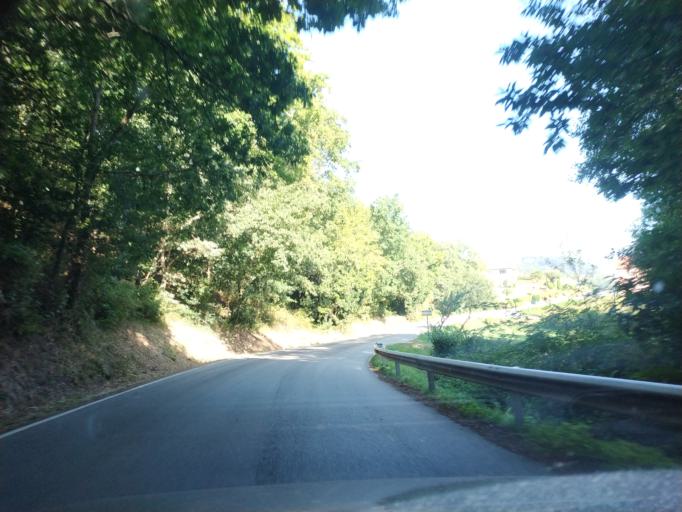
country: ES
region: Galicia
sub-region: Provincia da Coruna
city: Cerceda
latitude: 43.2339
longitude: -8.4819
